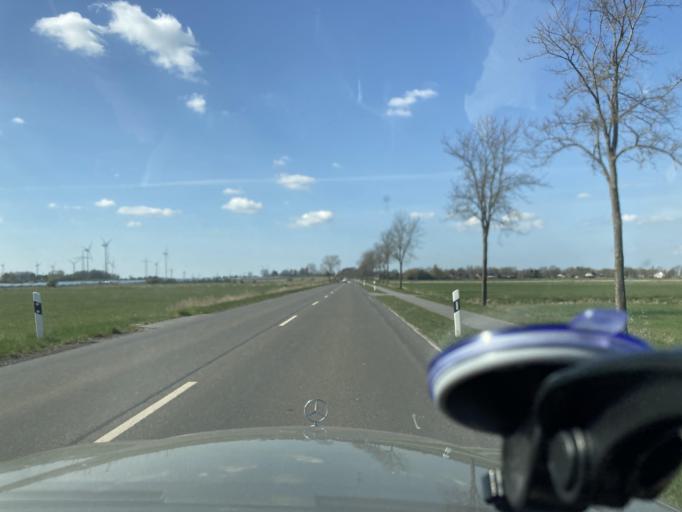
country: DE
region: Schleswig-Holstein
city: Weddingstedt
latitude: 54.2458
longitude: 9.0741
